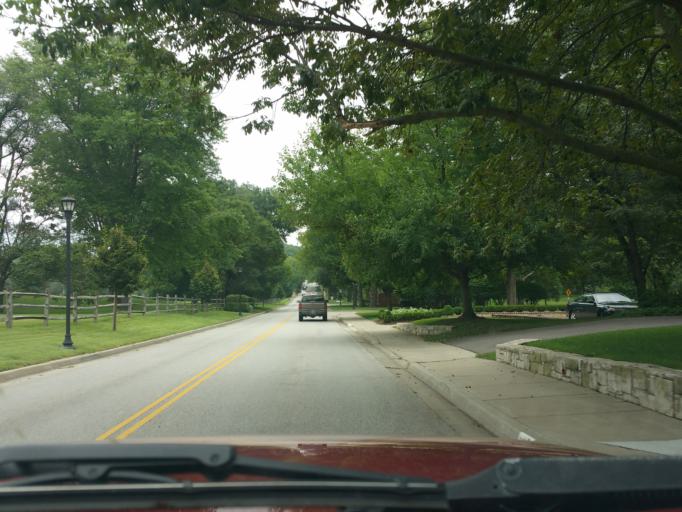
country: US
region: Kansas
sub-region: Johnson County
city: Mission Hills
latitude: 39.0151
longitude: -94.6251
